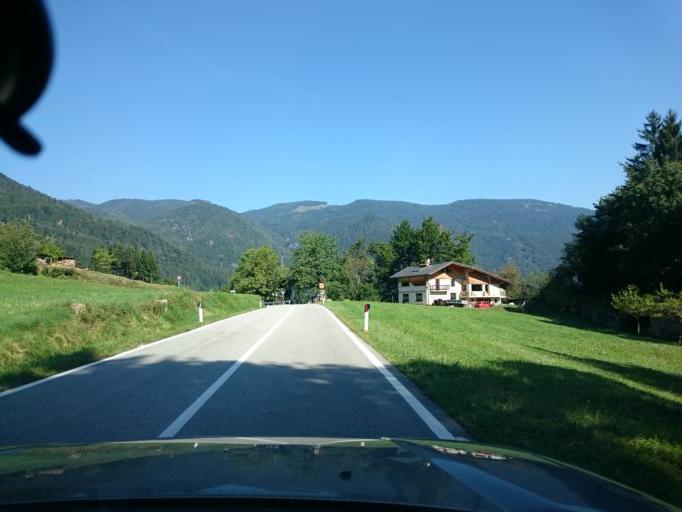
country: IT
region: Friuli Venezia Giulia
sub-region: Provincia di Udine
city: Tarvisio
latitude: 46.5066
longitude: 13.6139
